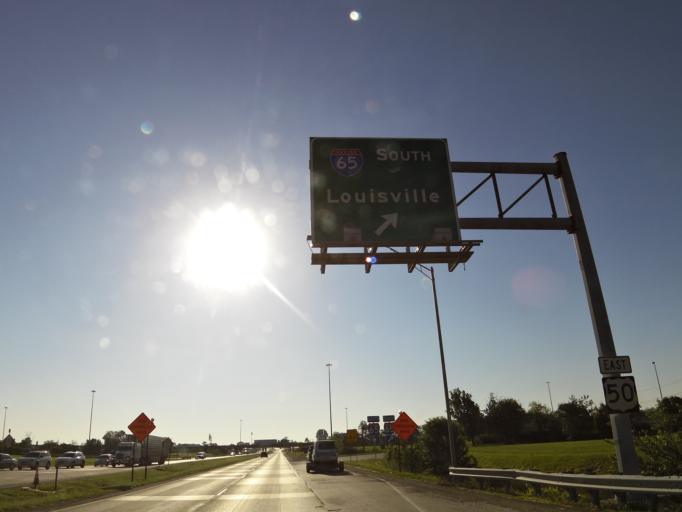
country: US
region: Indiana
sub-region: Jackson County
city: Seymour
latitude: 38.9579
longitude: -85.8483
